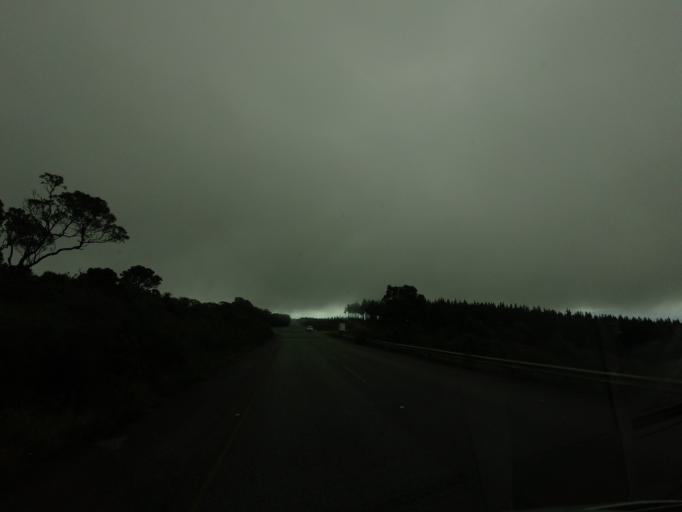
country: ZA
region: Mpumalanga
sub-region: Ehlanzeni District
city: Graksop
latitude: -24.8756
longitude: 30.8882
